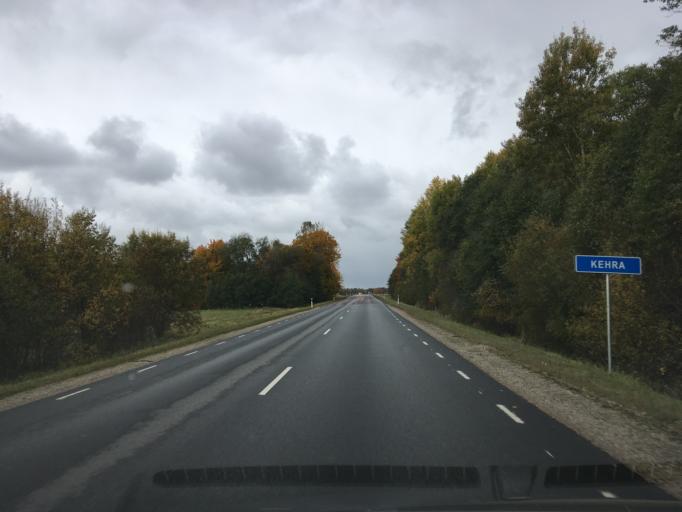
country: EE
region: Harju
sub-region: Anija vald
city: Kehra
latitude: 59.3251
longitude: 25.3313
